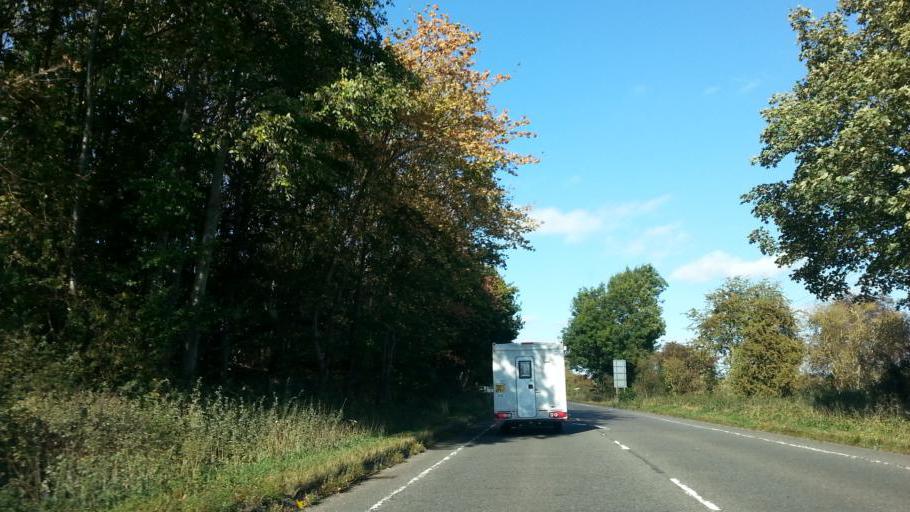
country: GB
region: England
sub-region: Northamptonshire
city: Oundle
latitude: 52.4797
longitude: -0.4576
